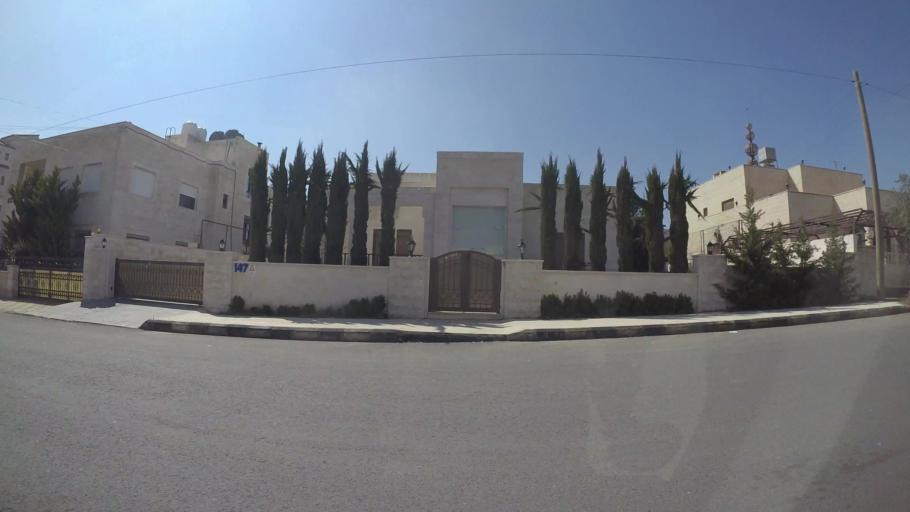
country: JO
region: Amman
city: Al Bunayyat ash Shamaliyah
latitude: 31.8977
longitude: 35.8863
